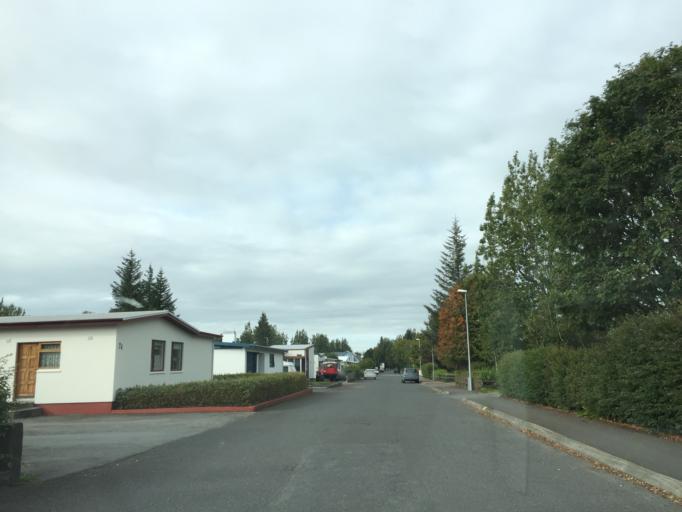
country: IS
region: South
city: Selfoss
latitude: 63.9353
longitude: -20.9873
